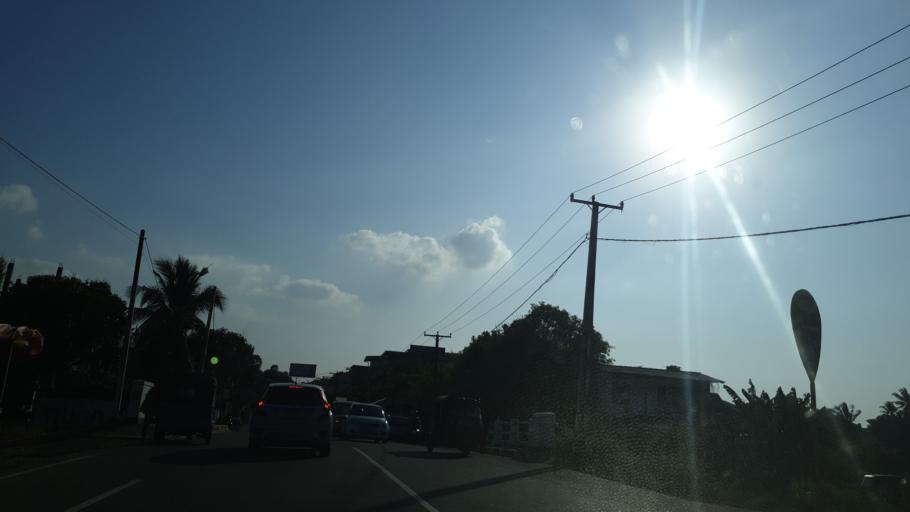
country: LK
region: Western
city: Sri Jayewardenepura Kotte
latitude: 6.8590
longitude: 79.8942
